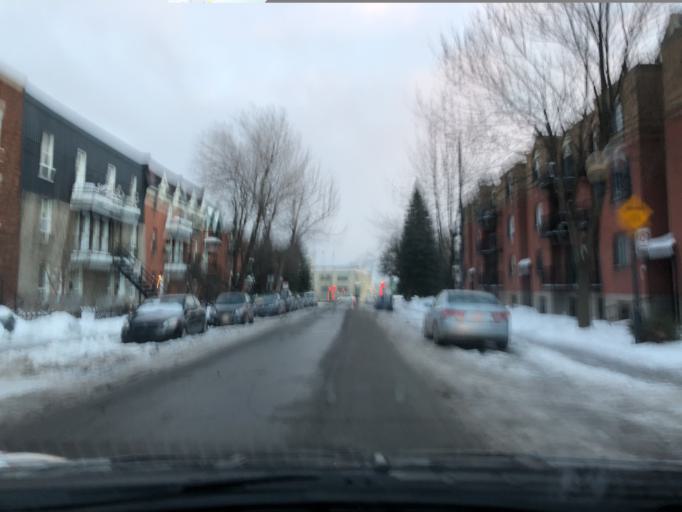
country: CA
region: Quebec
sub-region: Monteregie
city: Longueuil
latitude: 45.5410
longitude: -73.5398
